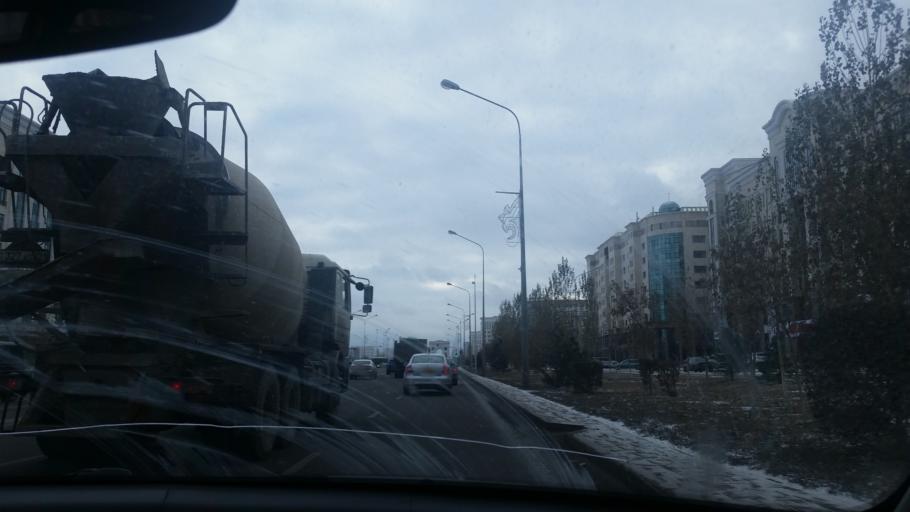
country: KZ
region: Astana Qalasy
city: Astana
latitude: 51.1112
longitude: 71.4324
